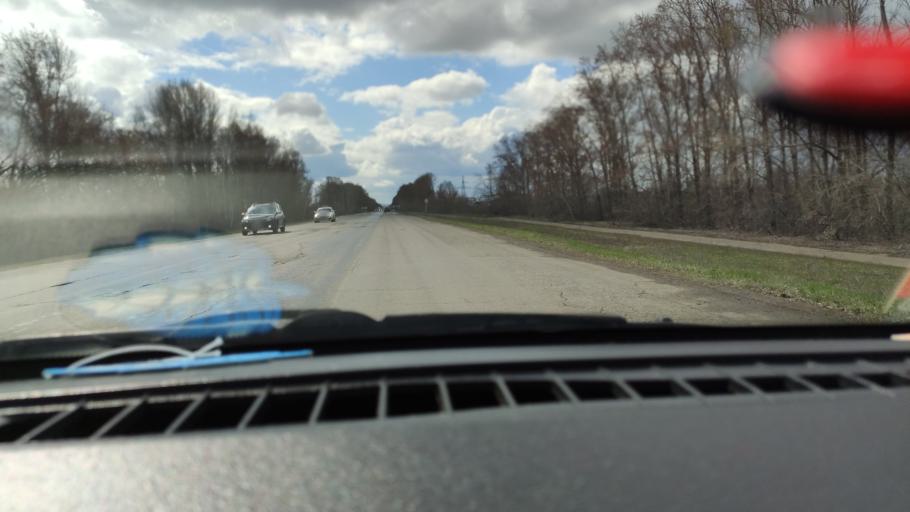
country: RU
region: Samara
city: Tol'yatti
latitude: 53.6305
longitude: 49.4173
